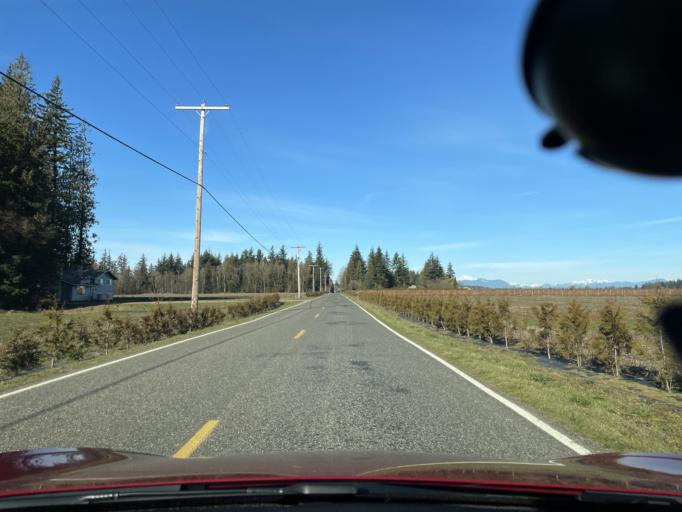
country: US
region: Washington
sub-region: Whatcom County
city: Lynden
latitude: 48.9526
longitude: -122.5303
